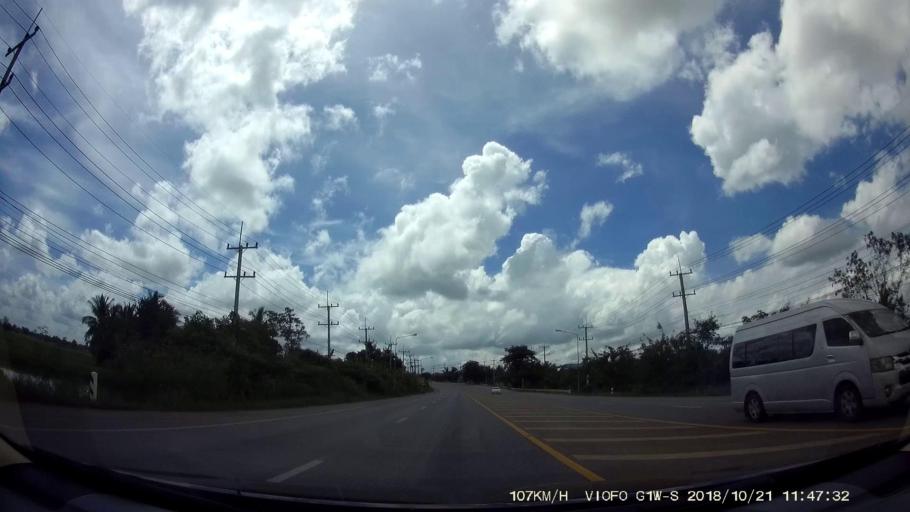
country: TH
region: Chaiyaphum
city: Noen Sa-nga
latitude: 15.6600
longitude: 101.9532
